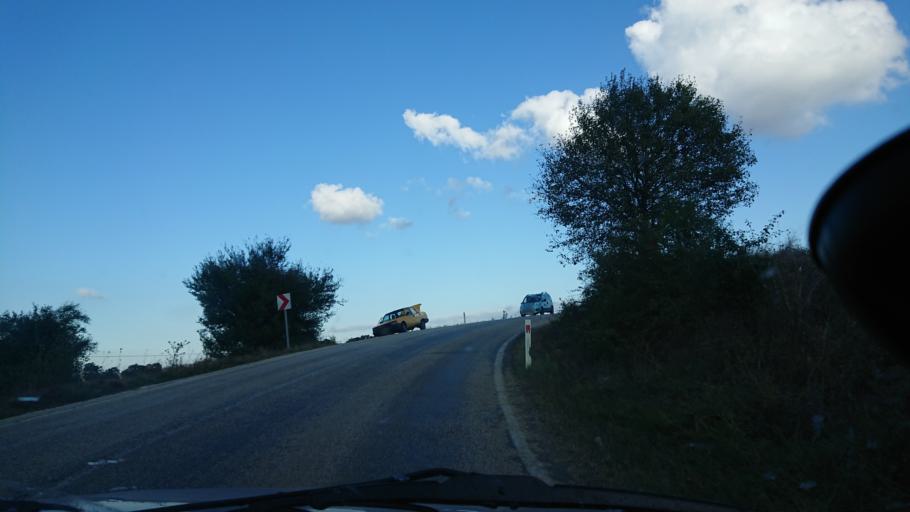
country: TR
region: Bilecik
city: Pazaryeri
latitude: 40.0085
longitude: 29.8698
